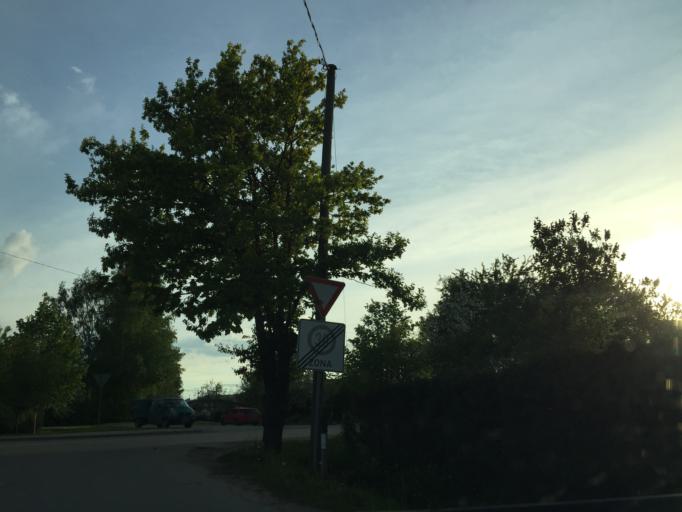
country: LV
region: Ozolnieku
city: Ozolnieki
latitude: 56.6532
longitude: 23.7613
